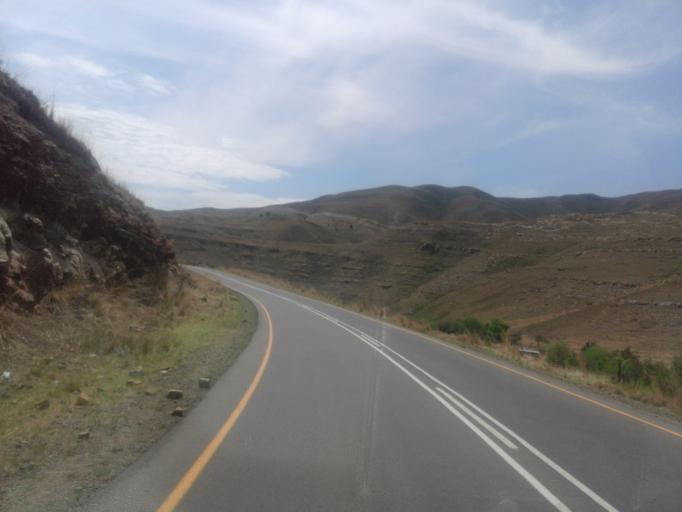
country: LS
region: Qacha's Nek
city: Qacha's Nek
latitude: -30.1019
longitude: 28.6565
